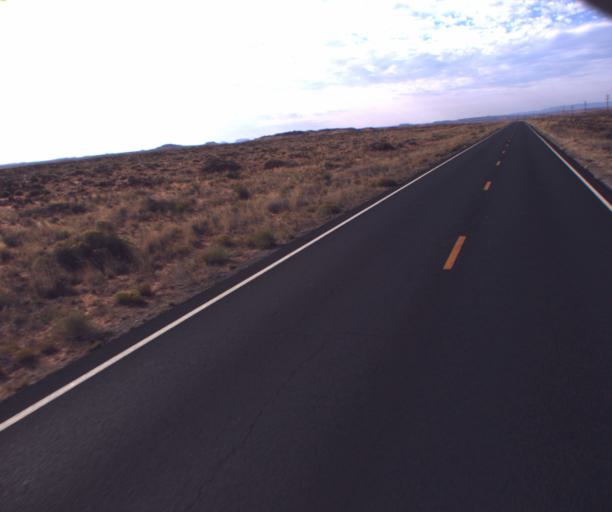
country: US
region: Arizona
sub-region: Apache County
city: Many Farms
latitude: 36.8472
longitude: -109.6396
